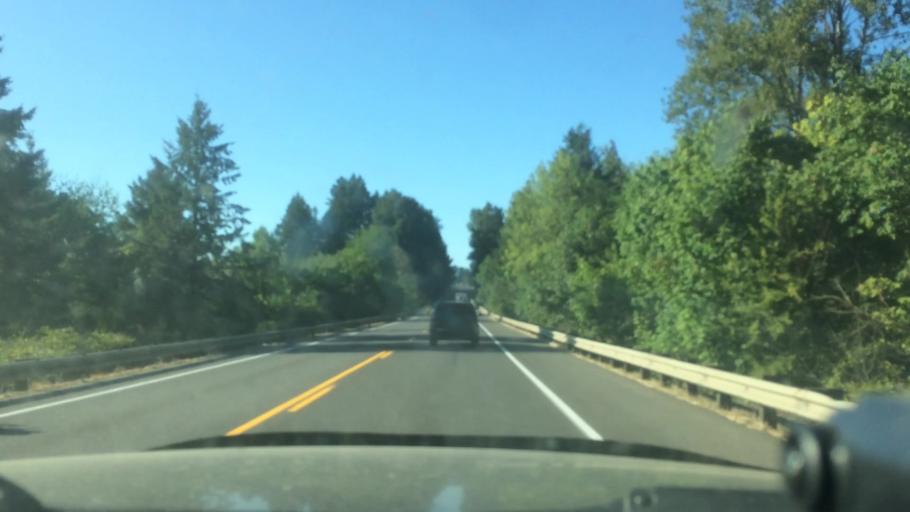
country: US
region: Oregon
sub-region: Yamhill County
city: Newberg
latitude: 45.2710
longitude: -122.9438
